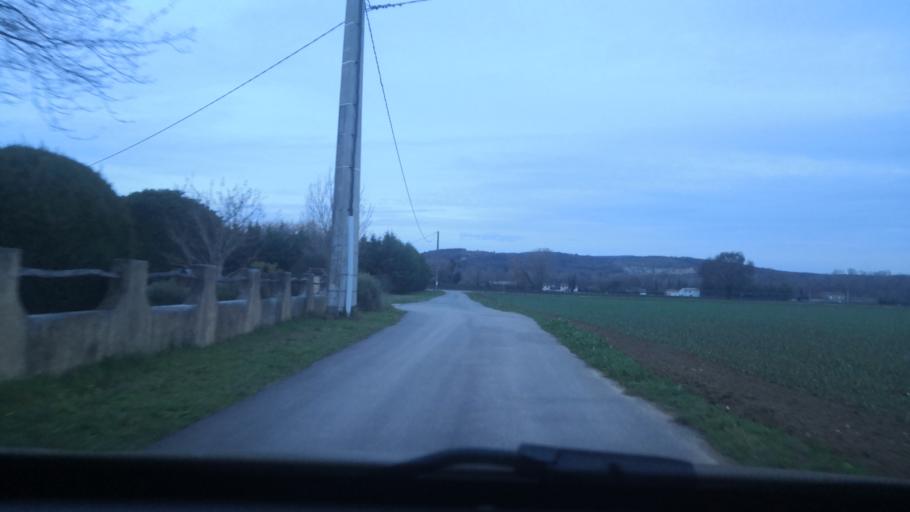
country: FR
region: Rhone-Alpes
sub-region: Departement de la Drome
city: Montboucher-sur-Jabron
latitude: 44.5536
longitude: 4.8393
